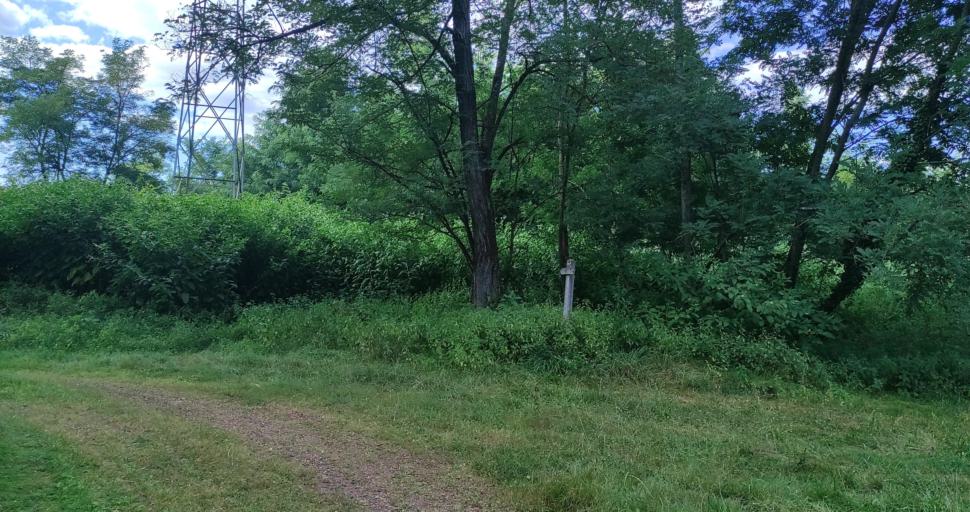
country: FR
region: Midi-Pyrenees
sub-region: Departement de l'Aveyron
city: Cransac
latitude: 44.5387
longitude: 2.2731
